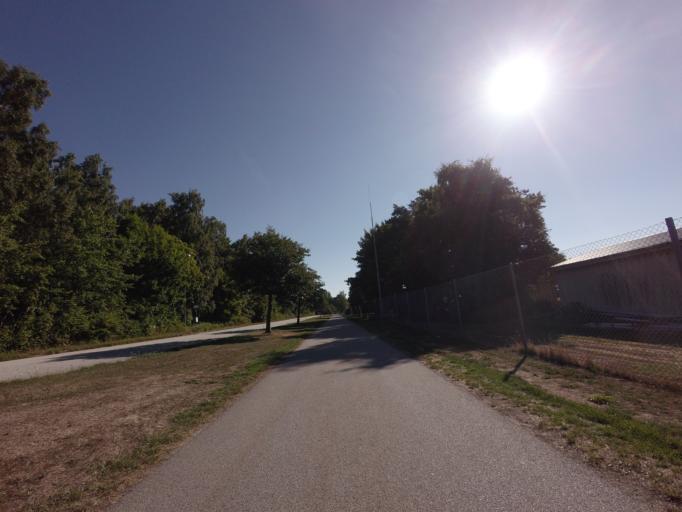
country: SE
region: Skane
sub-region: Ystads Kommun
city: Ystad
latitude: 55.4229
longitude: 13.8414
